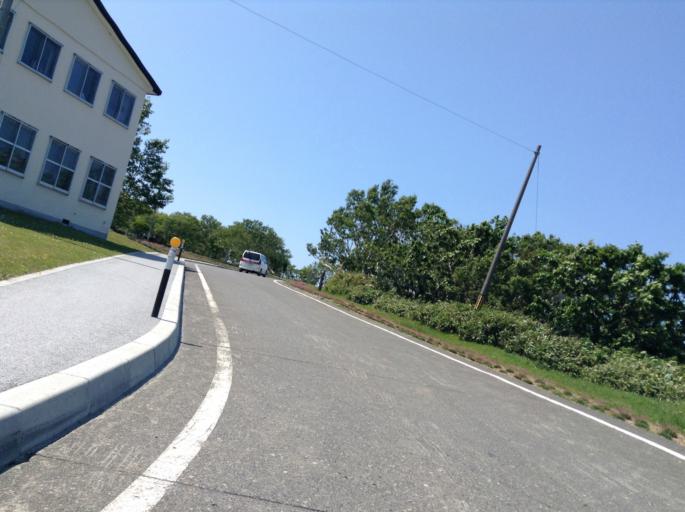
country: JP
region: Hokkaido
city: Wakkanai
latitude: 45.4203
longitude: 141.6691
